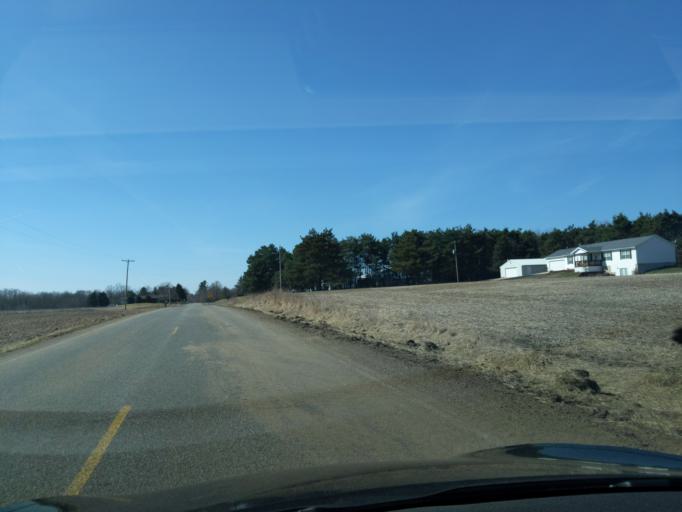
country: US
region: Michigan
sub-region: Ionia County
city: Lake Odessa
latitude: 42.7126
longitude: -85.0909
